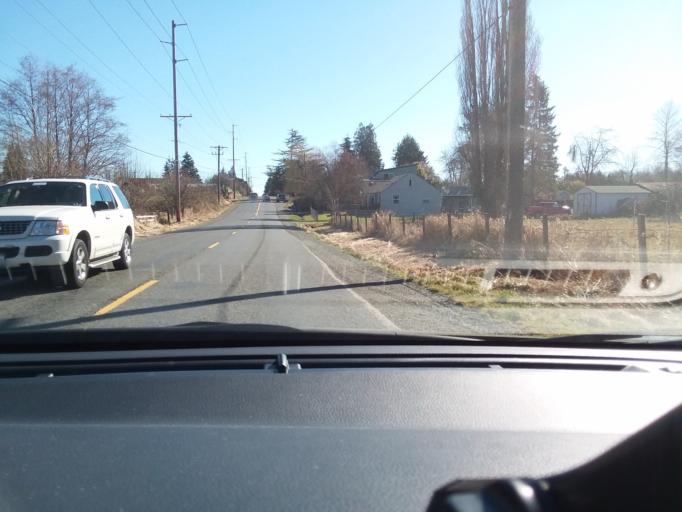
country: US
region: Washington
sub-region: Pierce County
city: Midland
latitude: 47.1699
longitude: -122.3924
